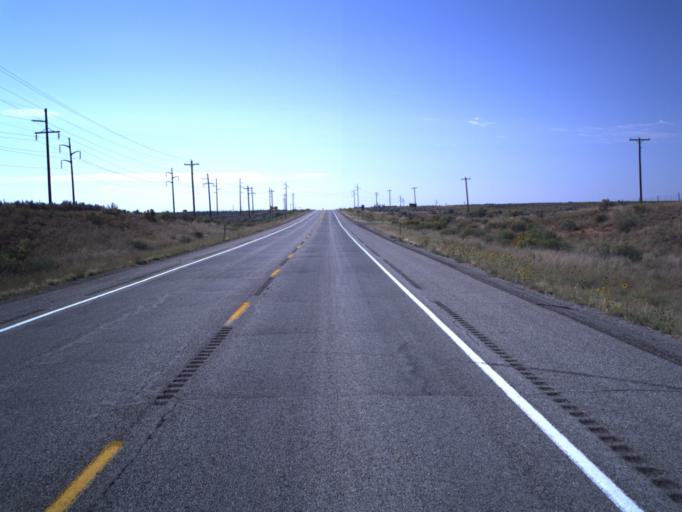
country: US
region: Utah
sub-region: San Juan County
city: Blanding
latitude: 37.5280
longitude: -109.4942
